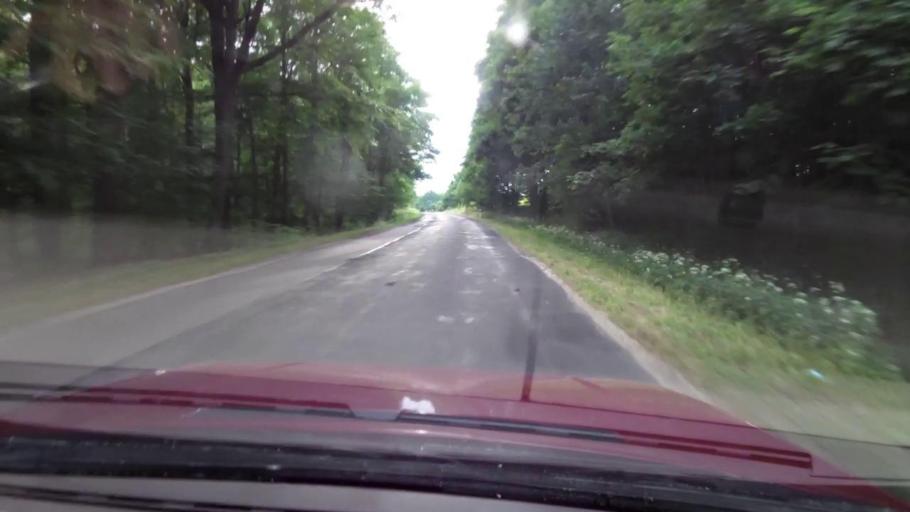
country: PL
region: Pomeranian Voivodeship
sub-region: Powiat bytowski
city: Trzebielino
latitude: 54.2700
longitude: 17.0206
